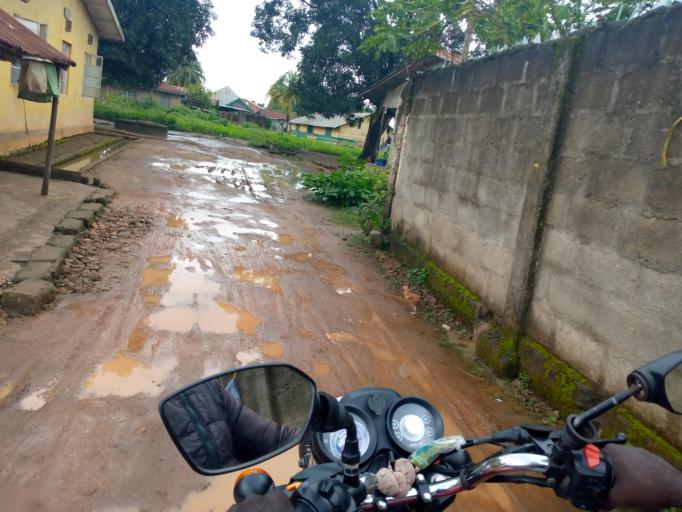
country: SL
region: Eastern Province
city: Kenema
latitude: 7.8842
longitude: -11.1786
